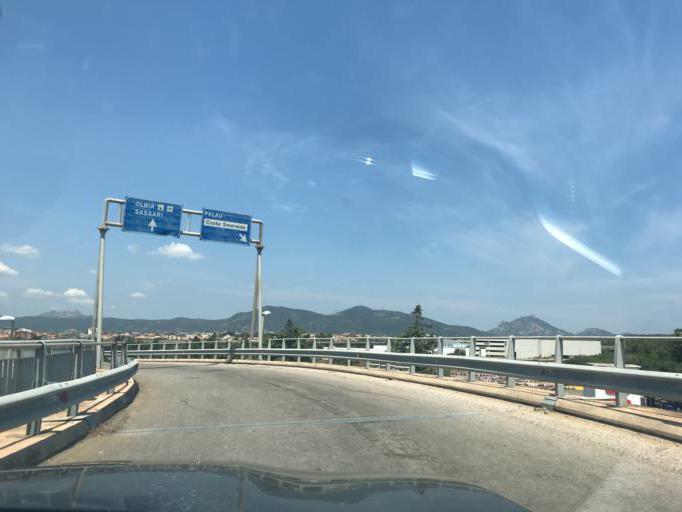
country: IT
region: Sardinia
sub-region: Provincia di Olbia-Tempio
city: Olbia
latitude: 40.9330
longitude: 9.5116
